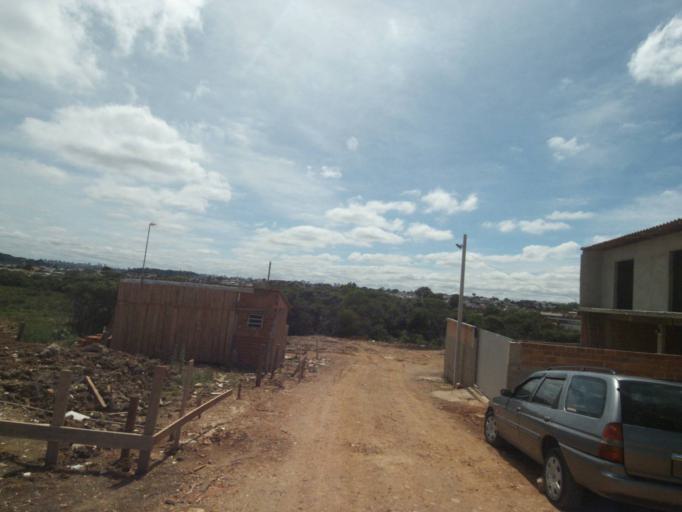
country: BR
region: Parana
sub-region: Curitiba
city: Curitiba
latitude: -25.4909
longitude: -49.3382
